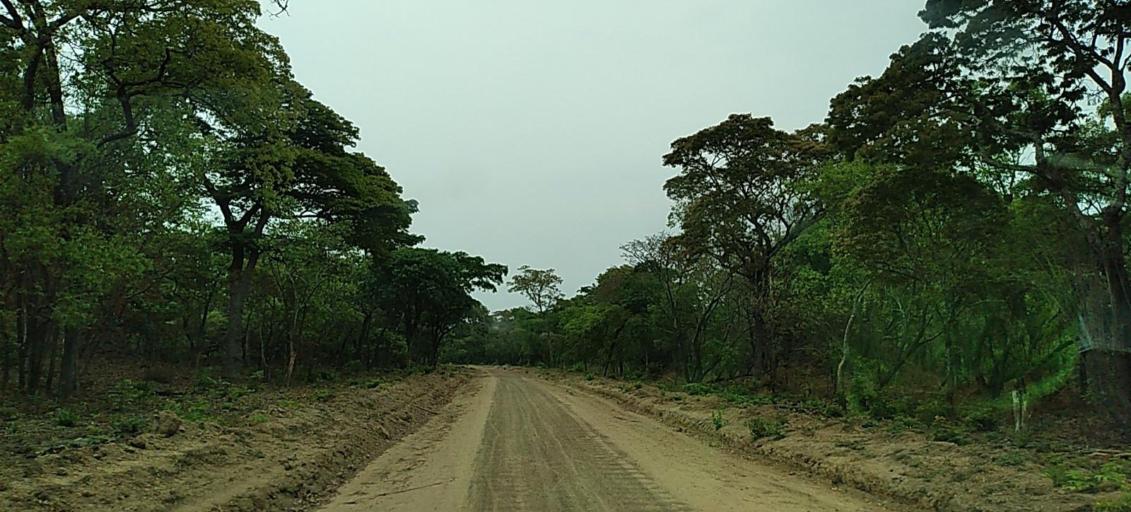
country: ZM
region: North-Western
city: Solwezi
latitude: -12.5197
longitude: 26.5244
